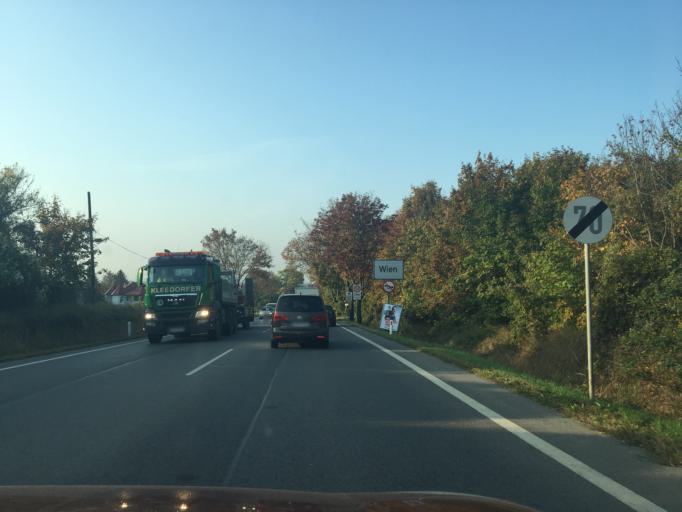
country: AT
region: Lower Austria
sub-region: Politischer Bezirk Korneuburg
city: Hagenbrunn
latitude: 48.3050
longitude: 16.4249
